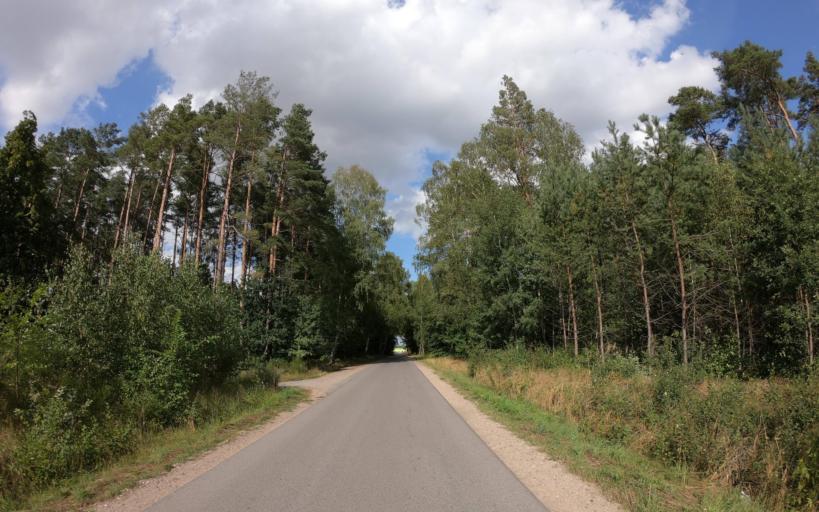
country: PL
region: West Pomeranian Voivodeship
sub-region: Powiat drawski
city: Wierzchowo
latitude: 53.4518
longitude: 16.0833
